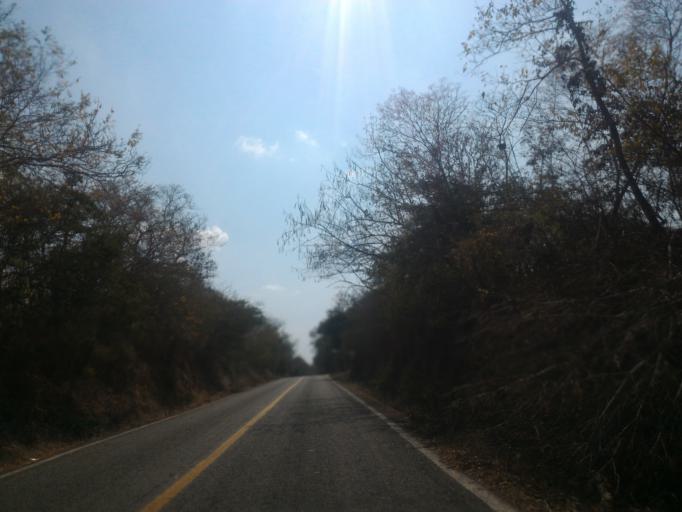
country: MX
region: Michoacan
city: Coahuayana Viejo
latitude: 18.3861
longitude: -103.5232
